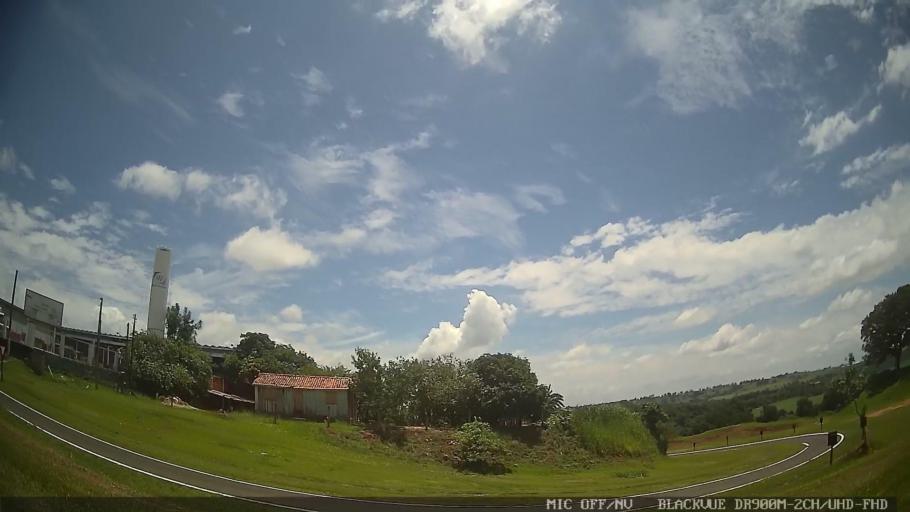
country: BR
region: Sao Paulo
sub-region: Laranjal Paulista
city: Laranjal Paulista
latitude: -23.0443
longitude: -47.8283
